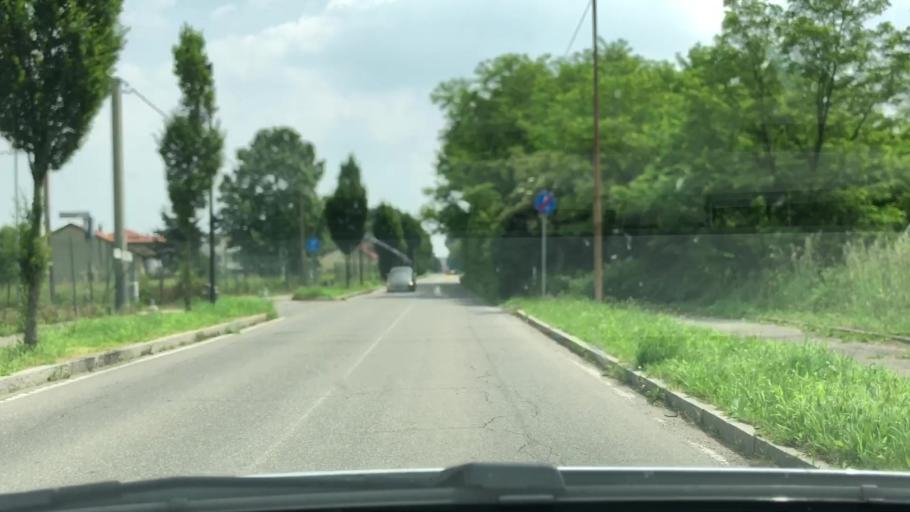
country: IT
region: Lombardy
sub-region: Provincia di Monza e Brianza
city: Desio
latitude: 45.6257
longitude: 9.1843
